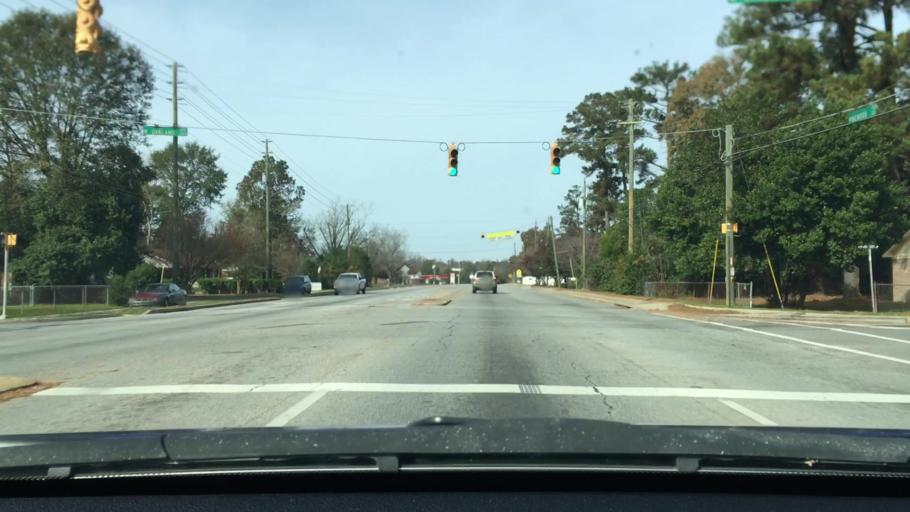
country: US
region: South Carolina
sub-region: Sumter County
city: South Sumter
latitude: 33.9112
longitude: -80.3823
